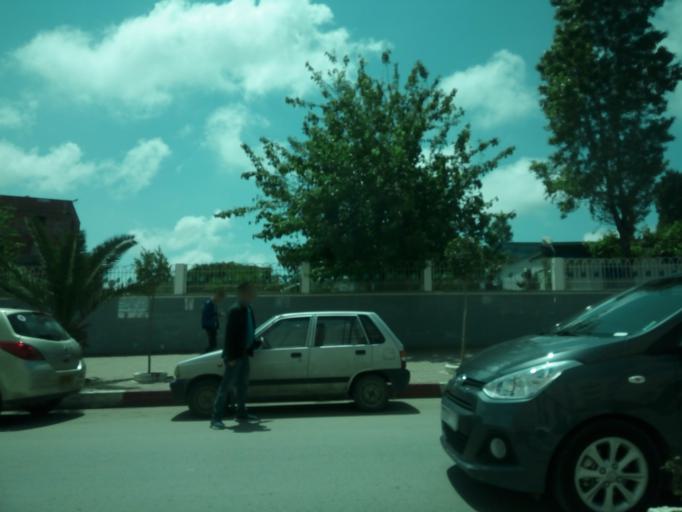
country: DZ
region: Tipaza
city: Saoula
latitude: 36.7236
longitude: 2.9910
